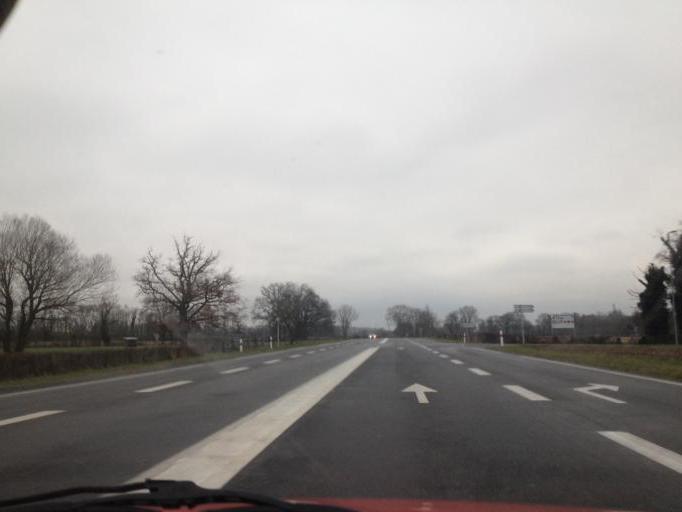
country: FR
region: Auvergne
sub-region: Departement de l'Allier
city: Varennes-sur-Allier
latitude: 46.2920
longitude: 3.4260
